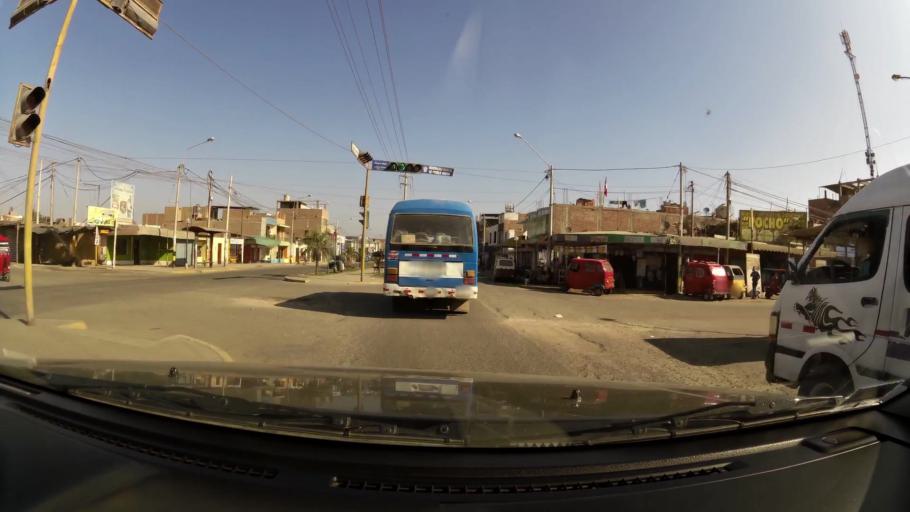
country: PE
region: Ica
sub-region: Provincia de Chincha
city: Chincha Alta
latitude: -13.4024
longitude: -76.1292
